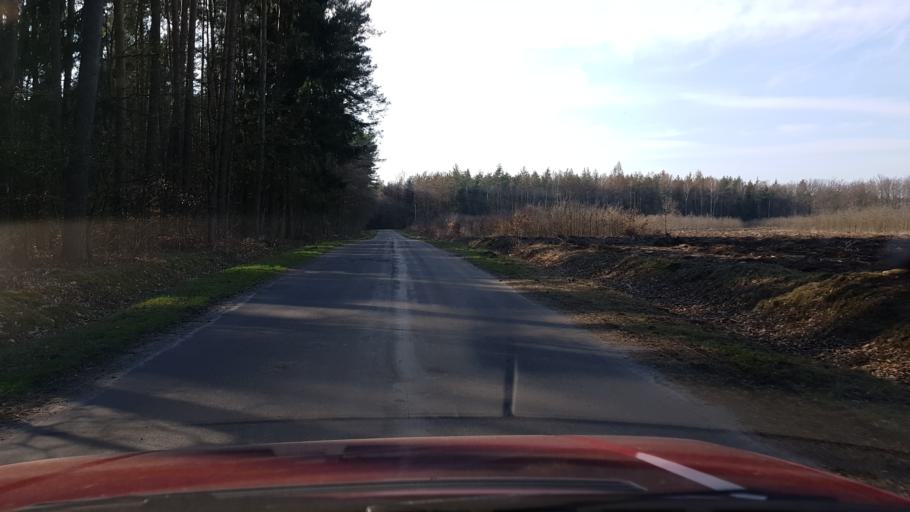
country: PL
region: West Pomeranian Voivodeship
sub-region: Powiat gryficki
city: Ploty
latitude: 53.8318
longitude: 15.3160
